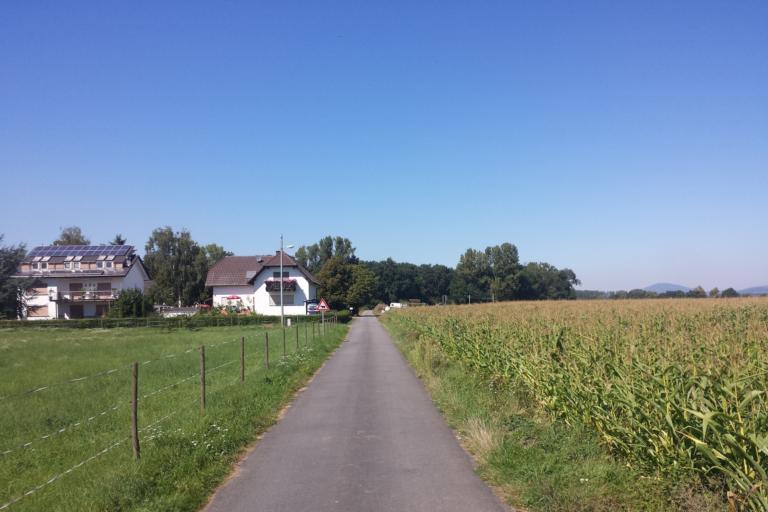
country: DE
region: Hesse
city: Viernheim
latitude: 49.5742
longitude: 8.5962
